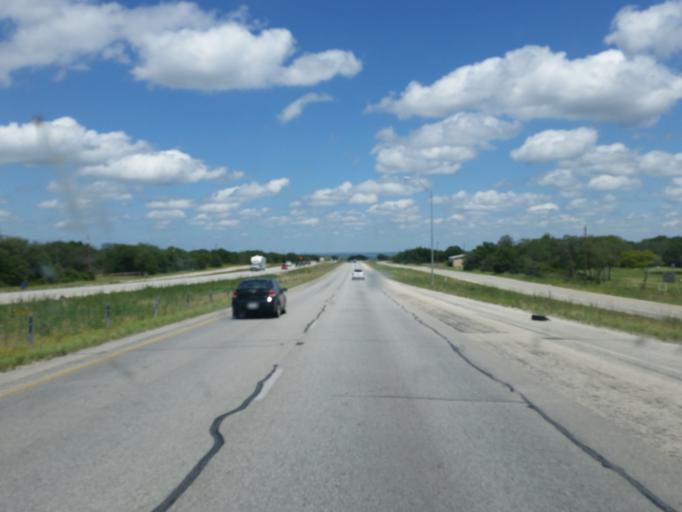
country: US
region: Texas
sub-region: Callahan County
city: Clyde
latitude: 32.4068
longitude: -99.4483
